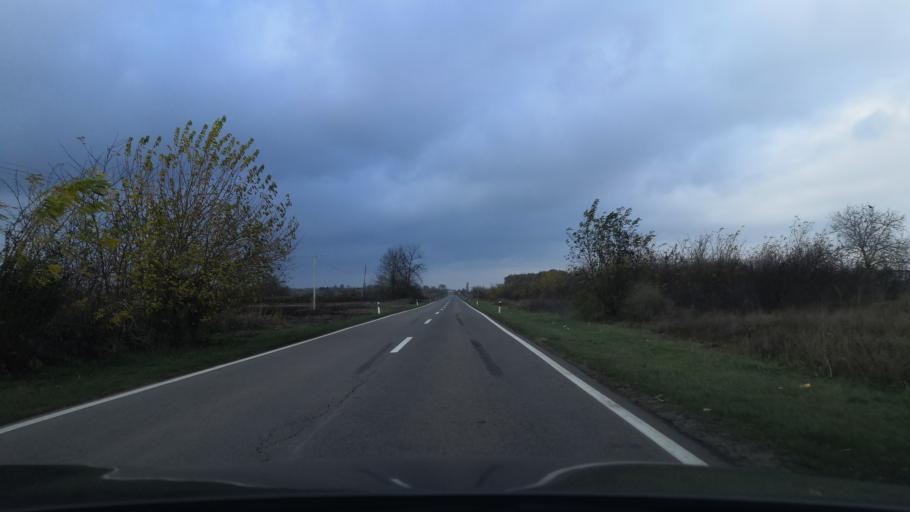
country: RS
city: Sanad
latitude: 45.9708
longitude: 20.1225
